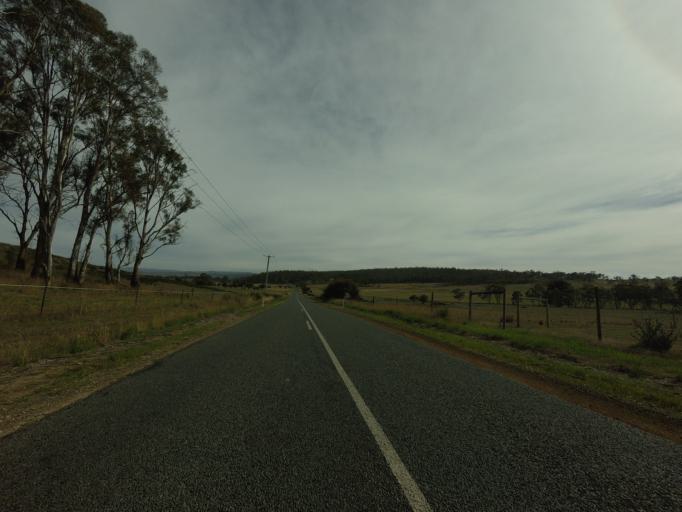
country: AU
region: Tasmania
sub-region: Brighton
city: Bridgewater
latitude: -42.3420
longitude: 147.4041
